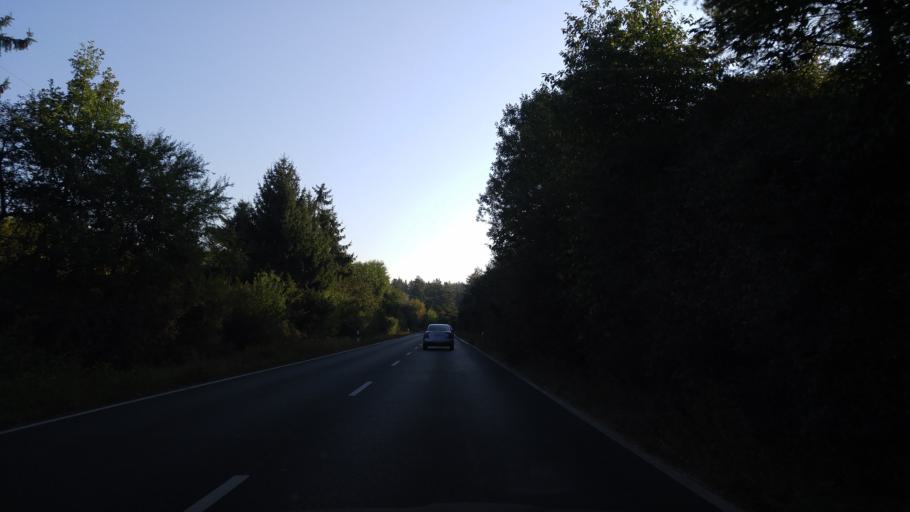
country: DE
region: Bavaria
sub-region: Regierungsbezirk Mittelfranken
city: Erlangen
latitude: 49.5561
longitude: 11.0188
